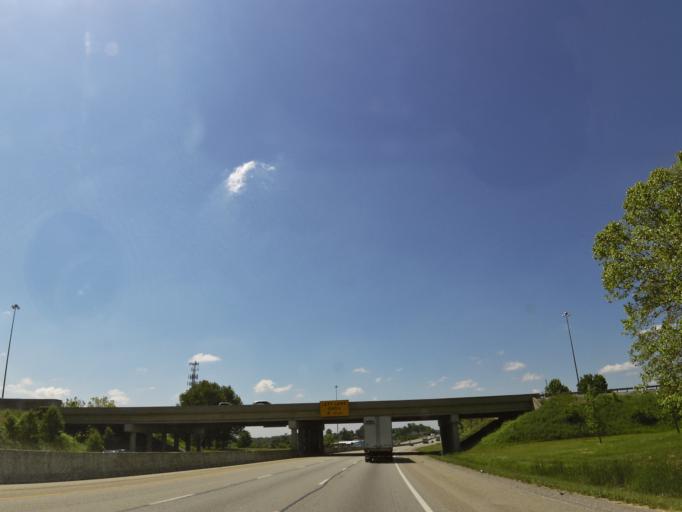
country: US
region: Kentucky
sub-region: Laurel County
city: London
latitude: 37.1114
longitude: -84.1026
